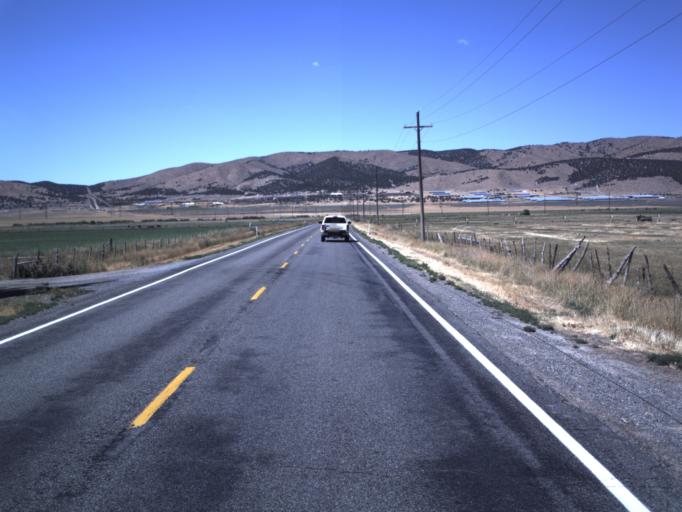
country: US
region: Utah
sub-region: Juab County
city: Nephi
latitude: 39.7101
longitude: -111.8854
